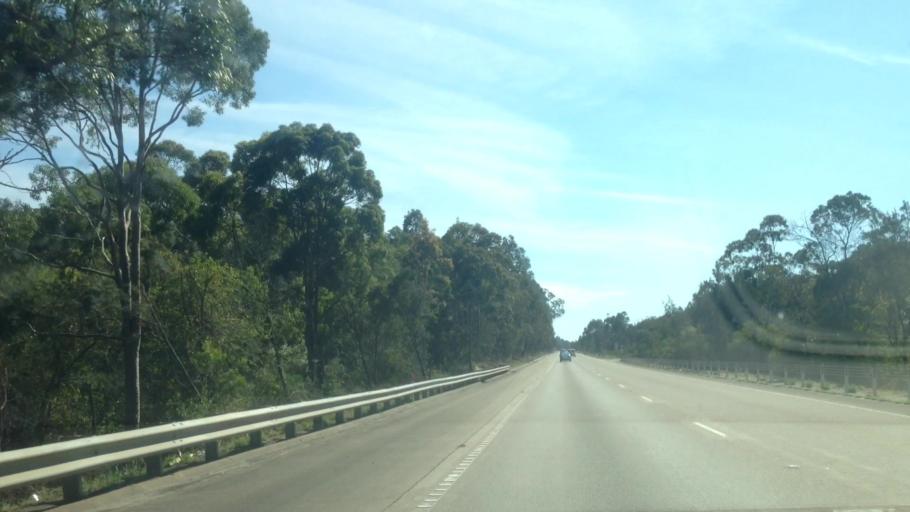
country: AU
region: New South Wales
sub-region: Lake Macquarie Shire
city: Fennell Bay
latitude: -32.9705
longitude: 151.5340
